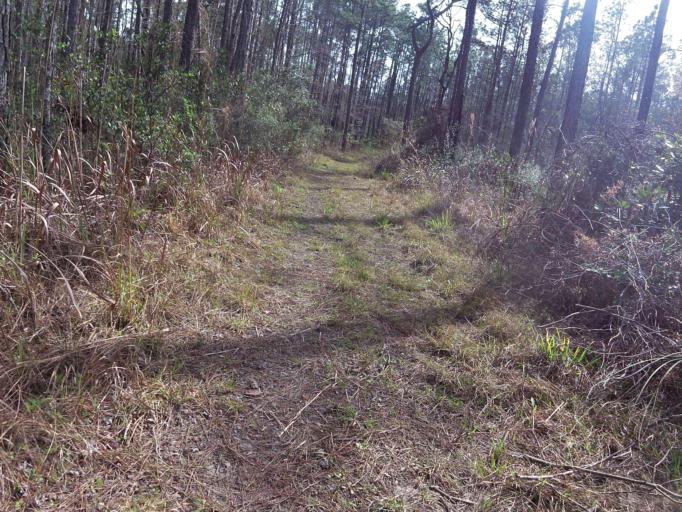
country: US
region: Florida
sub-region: Clay County
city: Middleburg
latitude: 30.1283
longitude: -81.9057
